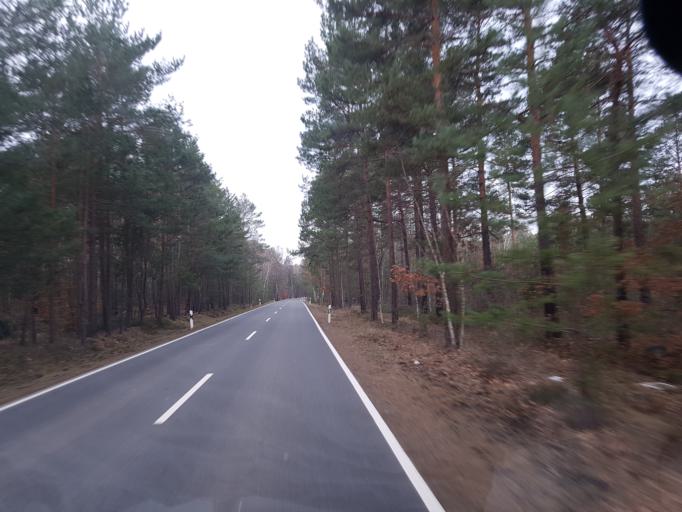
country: DE
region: Brandenburg
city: Sallgast
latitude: 51.5792
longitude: 13.8287
